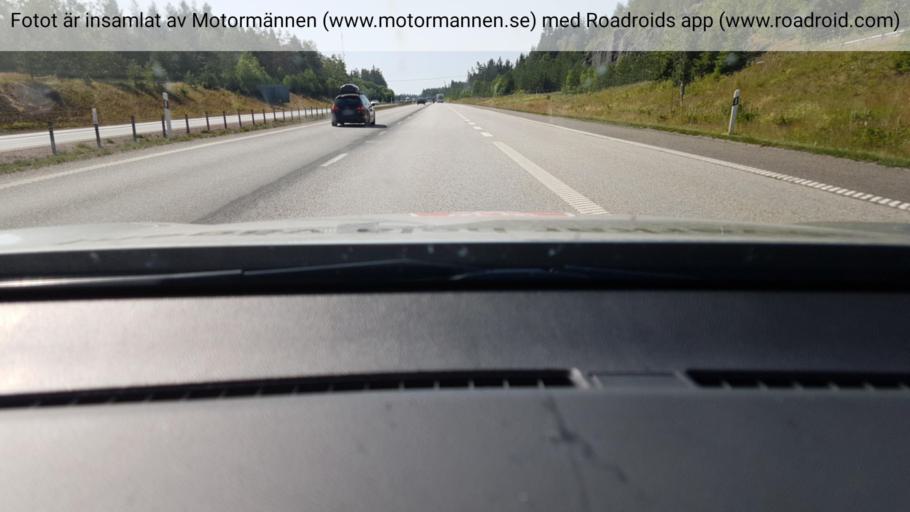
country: SE
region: Joenkoeping
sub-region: Jonkopings Kommun
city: Odensjo
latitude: 57.6600
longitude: 14.1781
